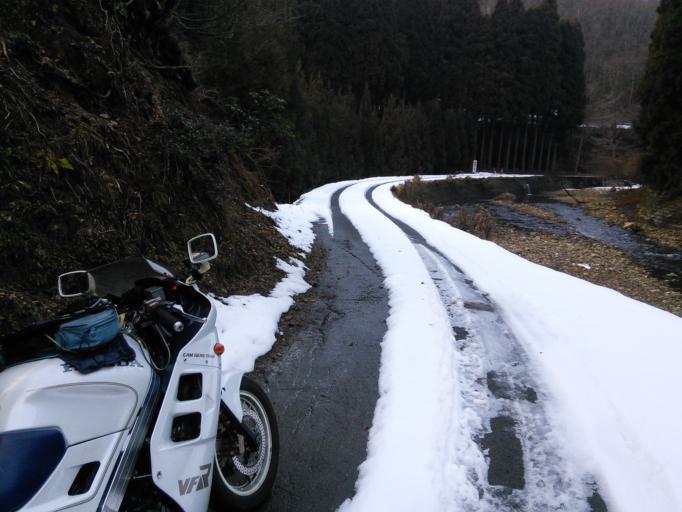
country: JP
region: Kyoto
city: Maizuru
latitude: 35.4028
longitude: 135.5053
